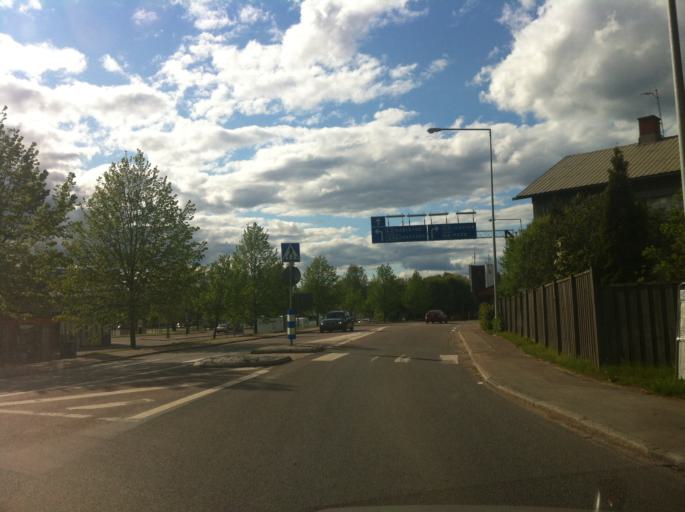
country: SE
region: Vaermland
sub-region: Filipstads Kommun
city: Filipstad
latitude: 59.6996
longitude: 14.1852
